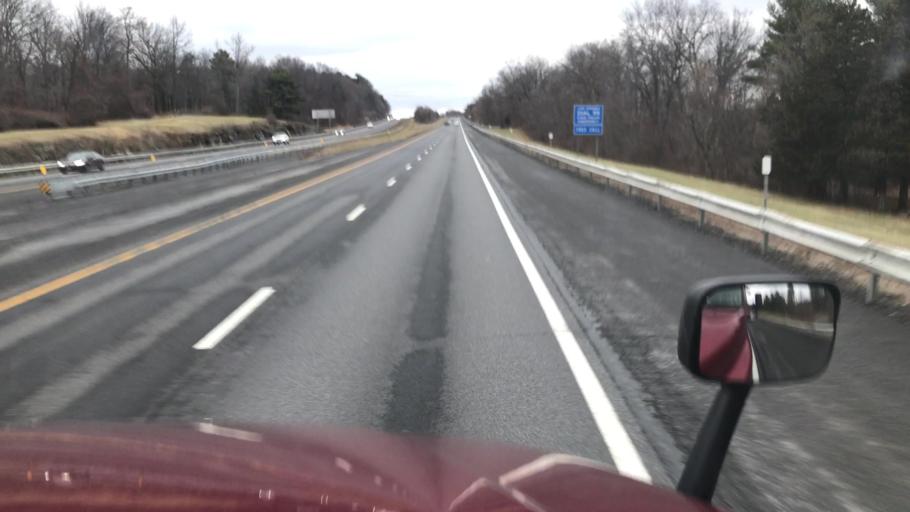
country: US
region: New York
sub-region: Greene County
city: Jefferson Heights
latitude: 42.2578
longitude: -73.8789
